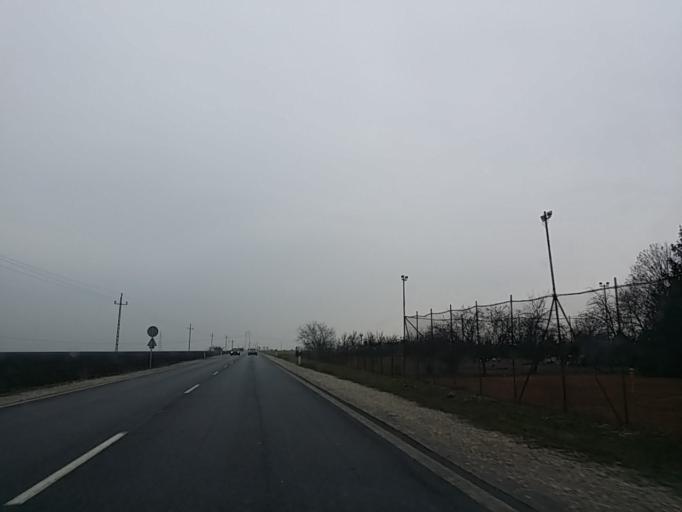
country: HU
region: Borsod-Abauj-Zemplen
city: Mezokeresztes
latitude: 47.8627
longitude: 20.6721
